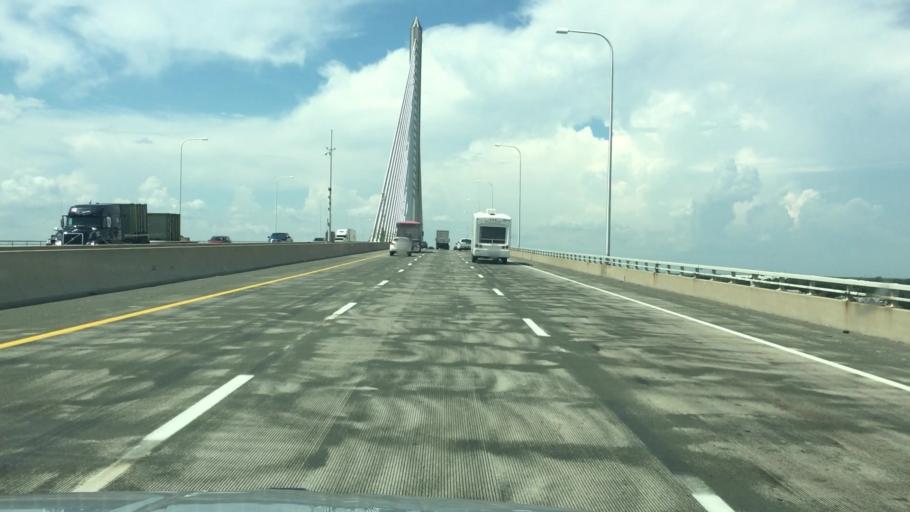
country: US
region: Ohio
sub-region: Lucas County
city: Oregon
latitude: 41.6584
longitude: -83.5097
